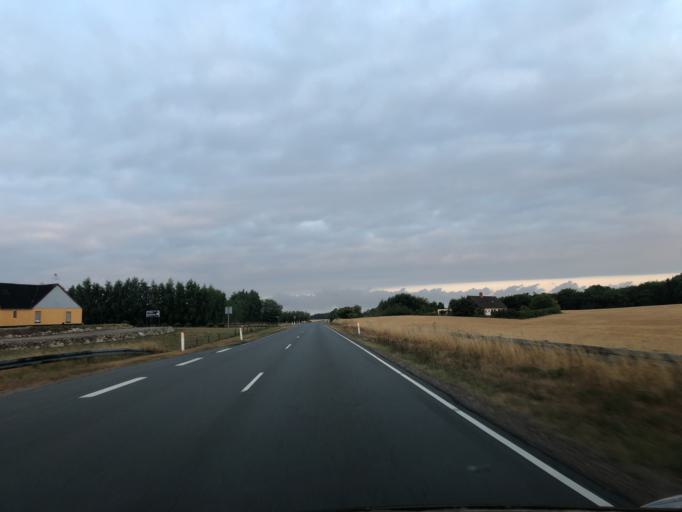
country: DK
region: Zealand
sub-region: Soro Kommune
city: Dianalund
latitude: 55.4672
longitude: 11.4735
